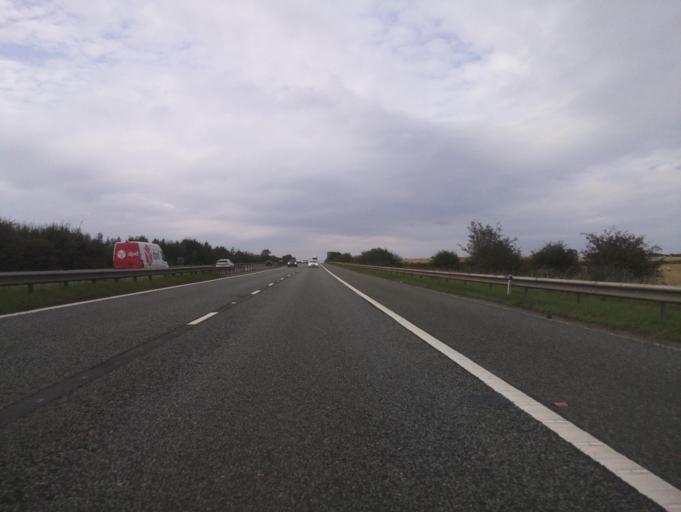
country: GB
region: England
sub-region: County Durham
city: Coxhoe
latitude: 54.7452
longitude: -1.5173
